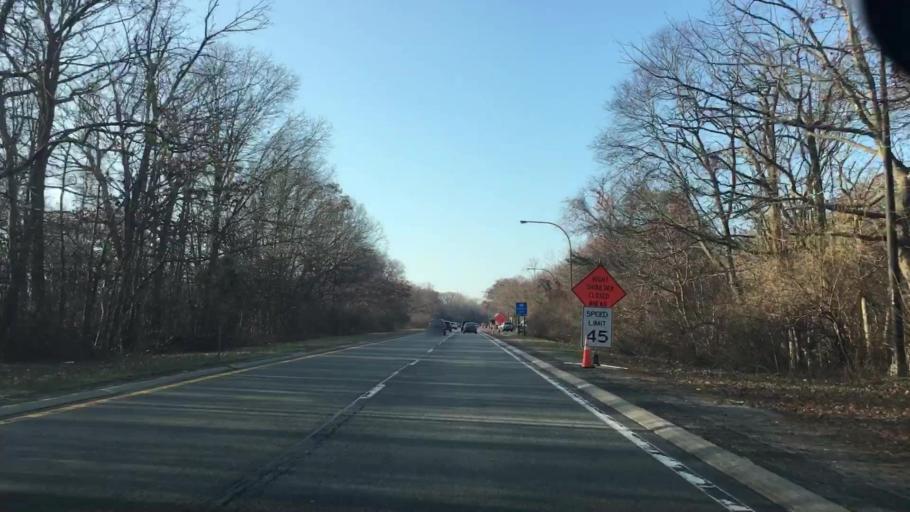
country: US
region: New York
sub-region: Suffolk County
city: Commack
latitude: 40.8227
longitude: -73.2644
